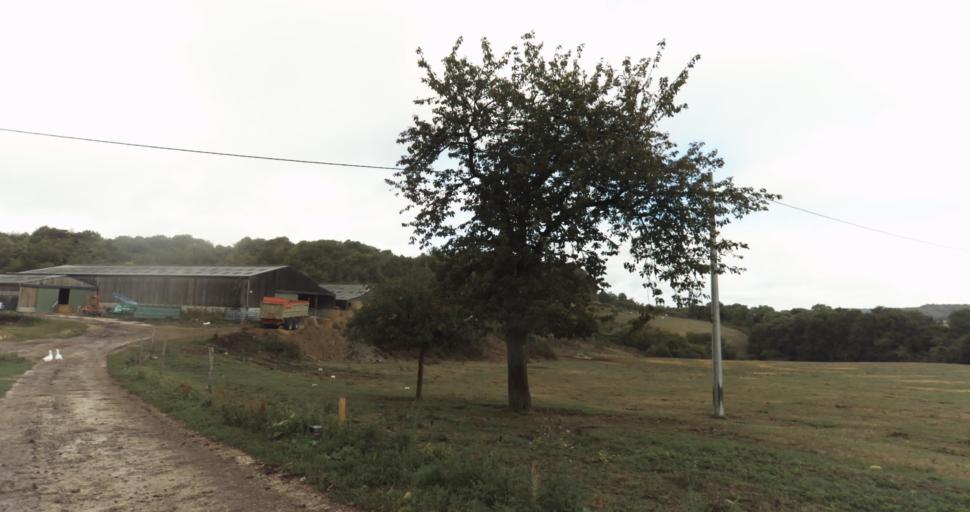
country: FR
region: Lower Normandy
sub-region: Departement de l'Orne
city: Vimoutiers
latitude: 48.8905
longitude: 0.2691
